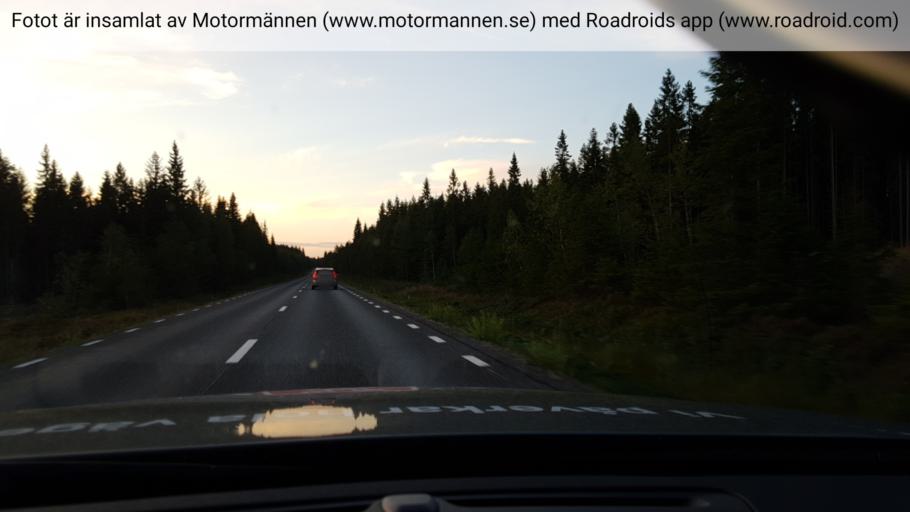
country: SE
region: OErebro
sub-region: Karlskoga Kommun
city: Karlskoga
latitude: 59.5152
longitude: 14.4925
